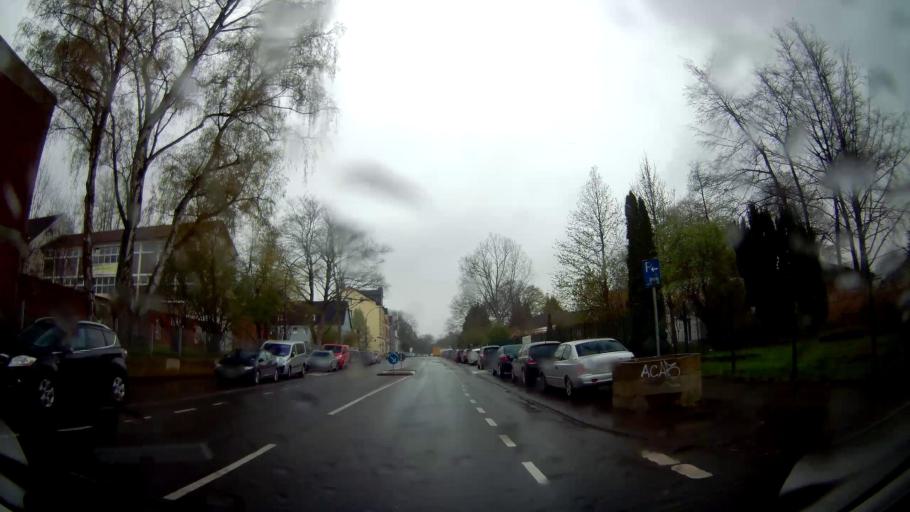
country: DE
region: North Rhine-Westphalia
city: Witten
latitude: 51.5071
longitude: 7.3713
